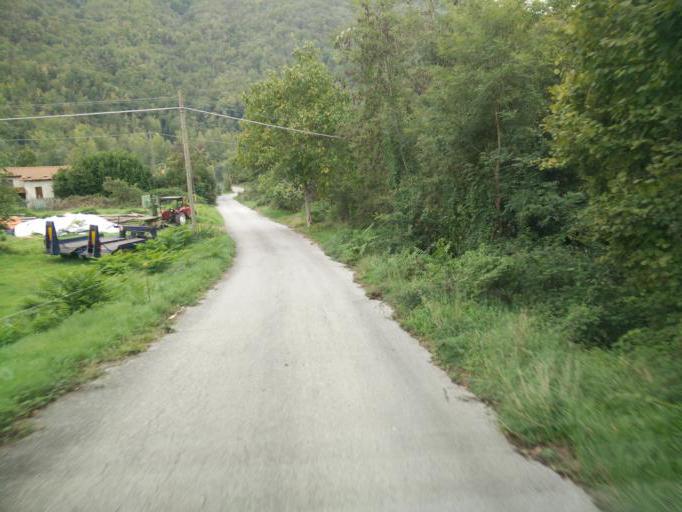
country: IT
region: Tuscany
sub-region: Provincia di Massa-Carrara
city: Casola in Lunigiana
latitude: 44.2003
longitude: 10.1732
